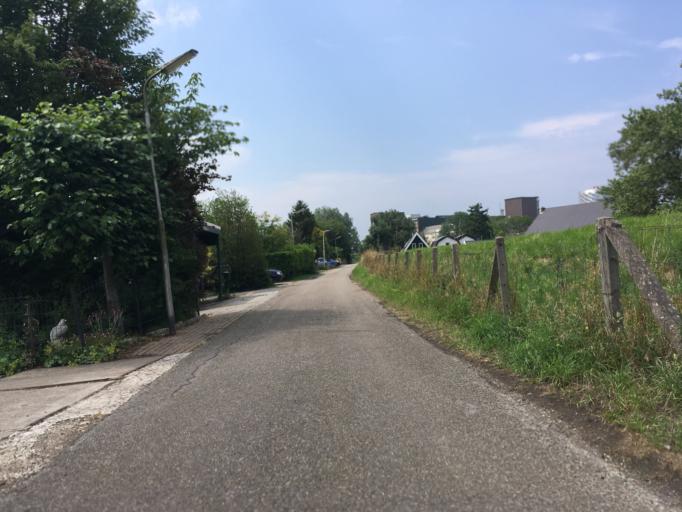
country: NL
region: North Holland
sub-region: Gemeente Zaanstad
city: Zaanstad
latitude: 52.3872
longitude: 4.7510
